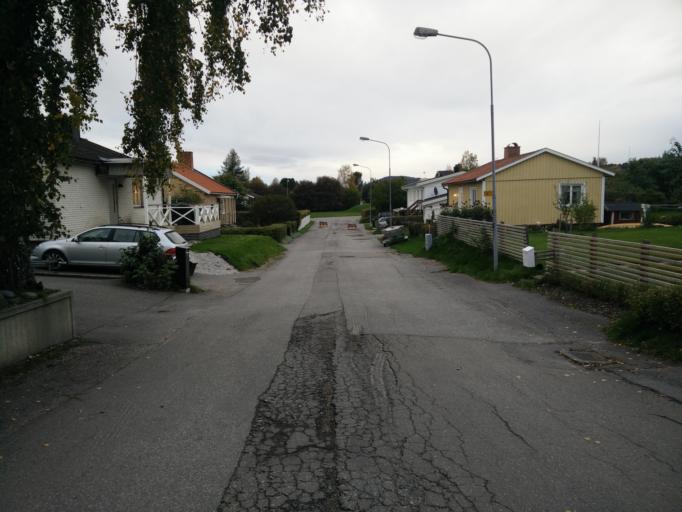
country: SE
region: Vaesternorrland
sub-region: Sundsvalls Kommun
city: Sundsvall
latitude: 62.3990
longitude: 17.2687
